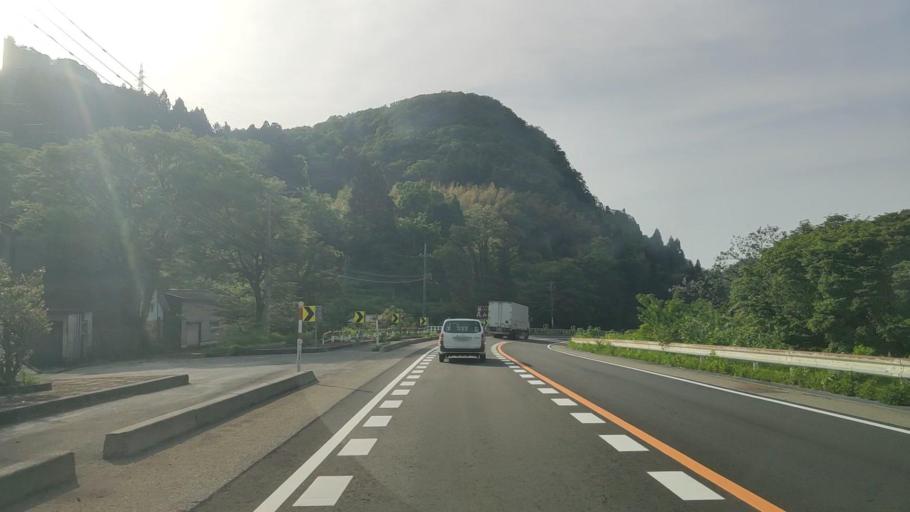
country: JP
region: Toyama
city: Yatsuomachi-higashikumisaka
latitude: 36.5471
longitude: 137.2263
